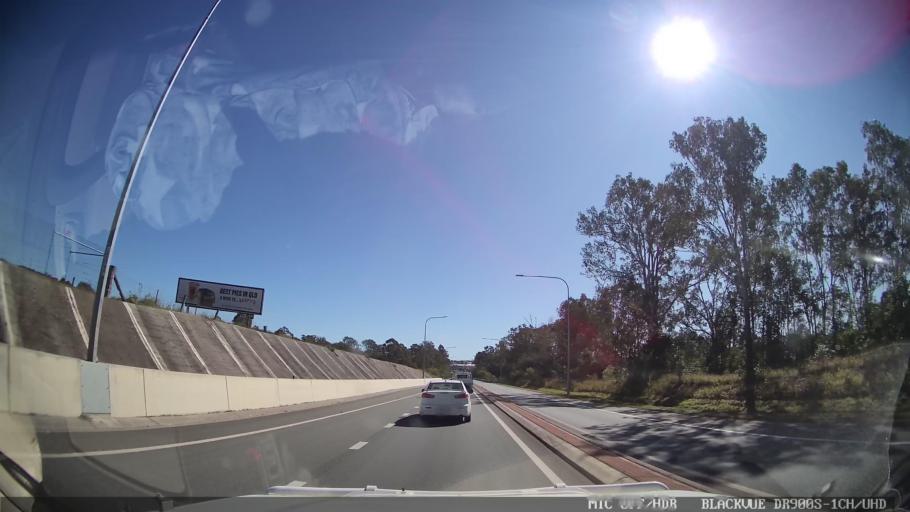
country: AU
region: Queensland
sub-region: Gympie Regional Council
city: Monkland
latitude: -26.2357
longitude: 152.6988
